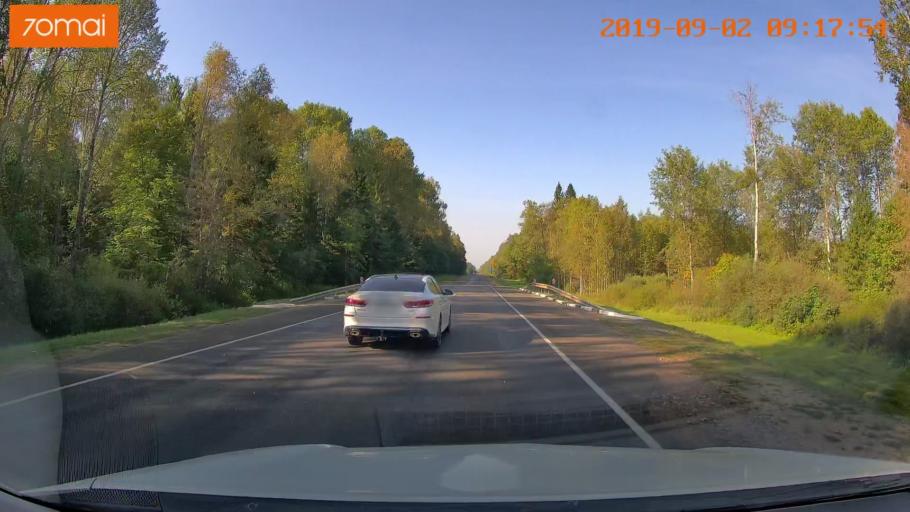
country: RU
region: Kaluga
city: Nikola-Lenivets
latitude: 54.8205
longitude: 35.4410
